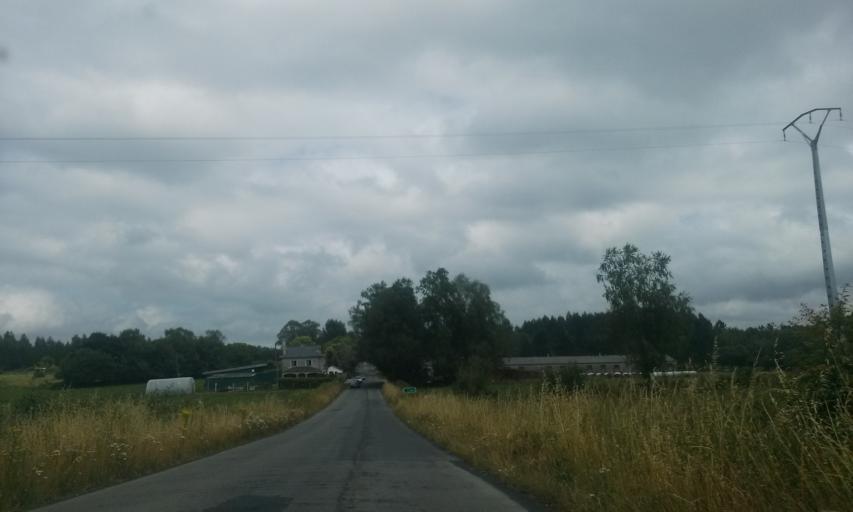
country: ES
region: Galicia
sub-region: Provincia de Lugo
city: Friol
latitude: 43.0905
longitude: -7.8095
